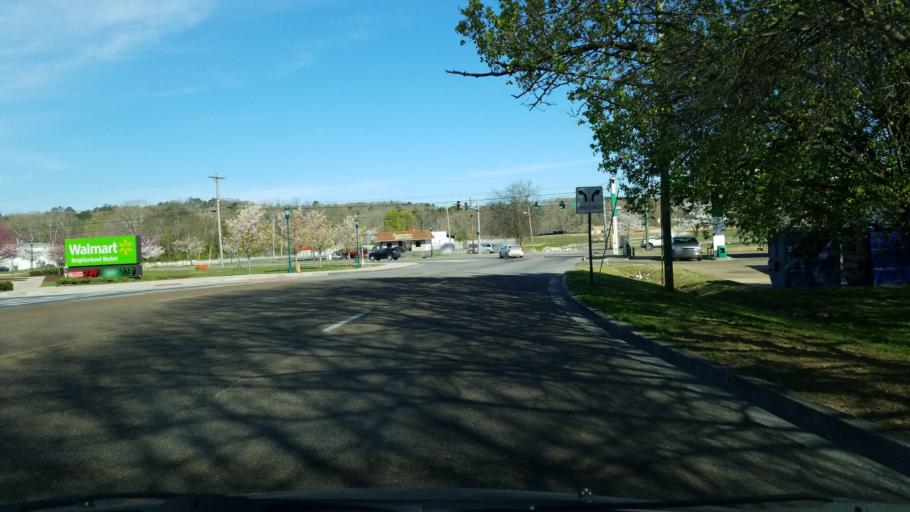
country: US
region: Tennessee
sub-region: Hamilton County
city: East Chattanooga
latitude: 35.0427
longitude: -85.2192
